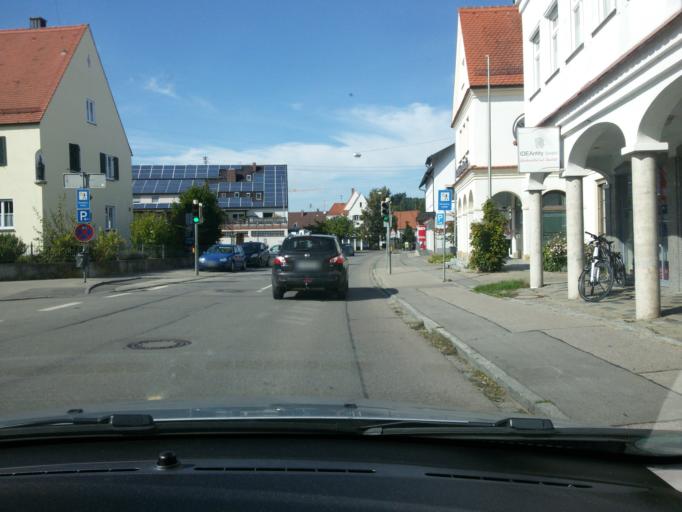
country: DE
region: Bavaria
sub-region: Swabia
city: Fischach
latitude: 48.2891
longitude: 10.6561
